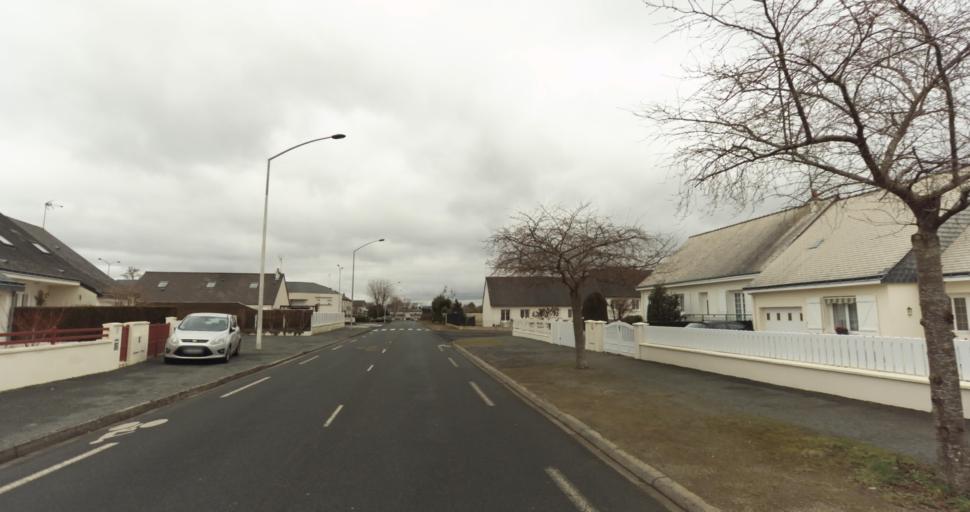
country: FR
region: Pays de la Loire
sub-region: Departement de Maine-et-Loire
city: Distre
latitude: 47.2383
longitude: -0.0918
